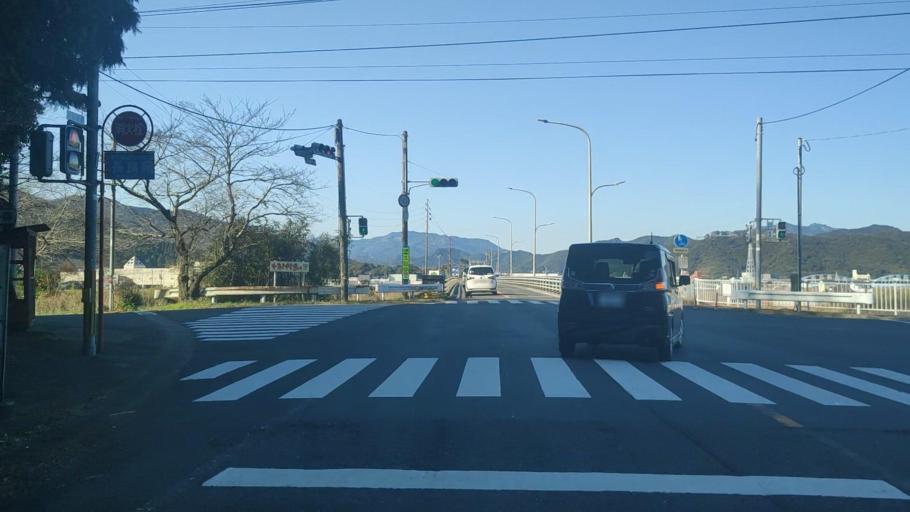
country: JP
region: Oita
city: Saiki
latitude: 32.9431
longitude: 131.9078
